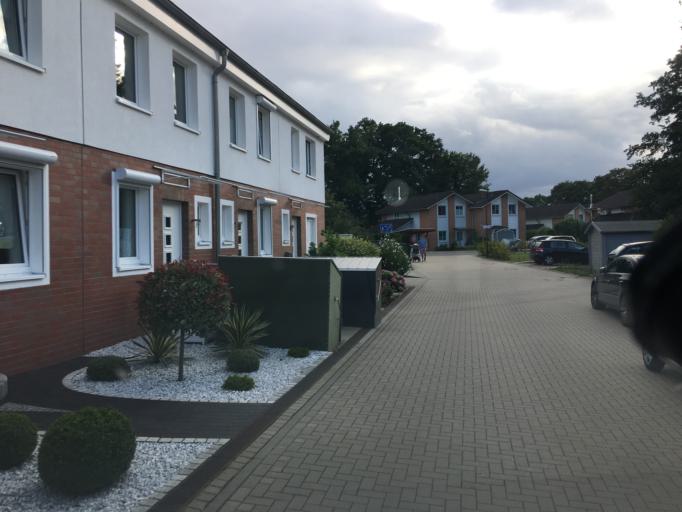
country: DE
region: Lower Saxony
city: Neu Wulmstorf
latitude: 53.4842
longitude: 9.8650
